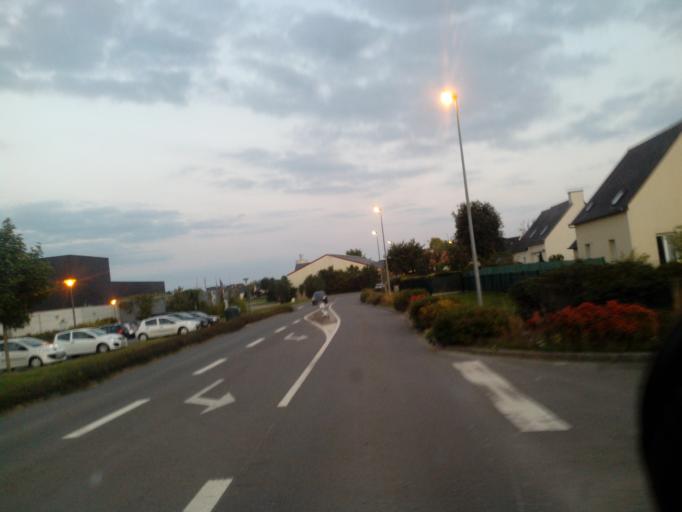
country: FR
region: Brittany
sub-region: Departement d'Ille-et-Vilaine
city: Montfort-sur-Meu
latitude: 48.1447
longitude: -1.9669
